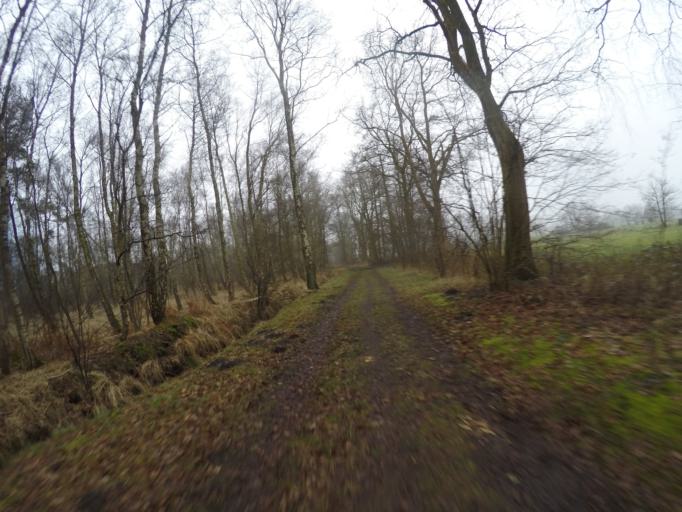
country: DE
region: Schleswig-Holstein
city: Quickborn
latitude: 53.7146
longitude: 9.9254
